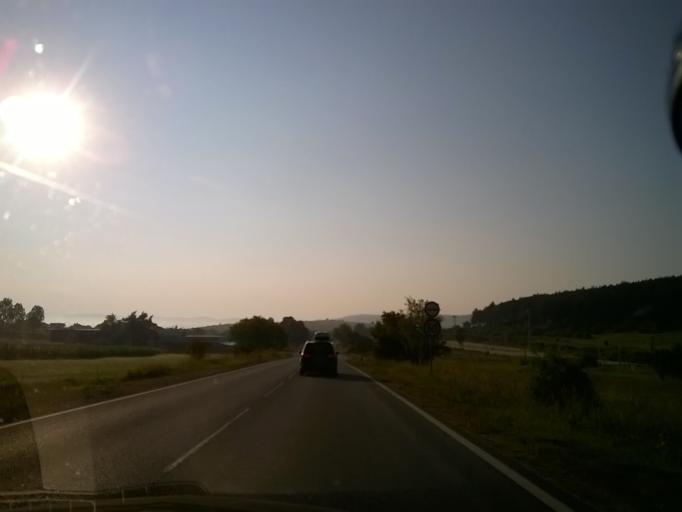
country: BG
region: Sofiya
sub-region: Obshtina Dragoman
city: Dragoman
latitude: 42.9318
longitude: 22.9243
